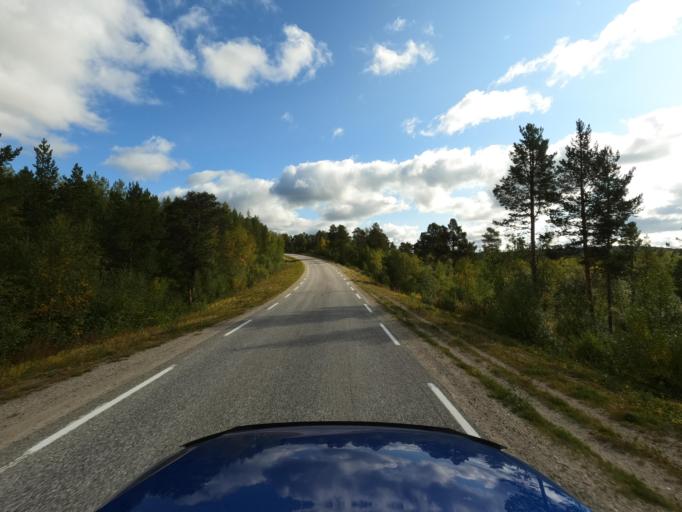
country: NO
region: Finnmark Fylke
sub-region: Karasjok
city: Karasjohka
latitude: 69.4431
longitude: 25.2712
